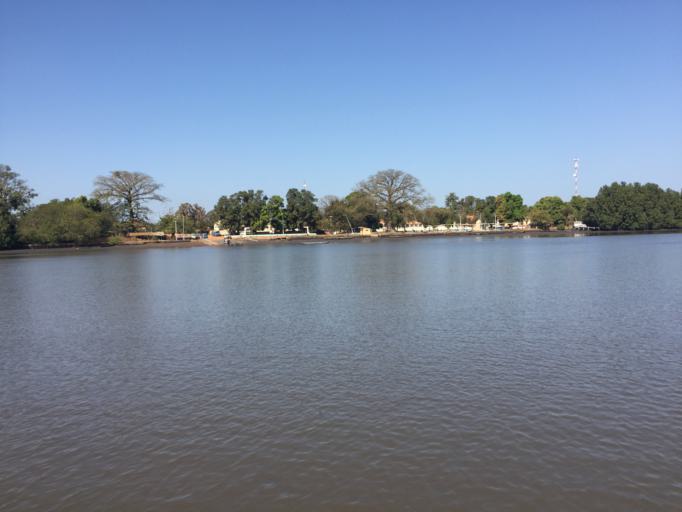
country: GW
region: Oio
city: Farim
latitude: 12.4776
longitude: -15.2225
